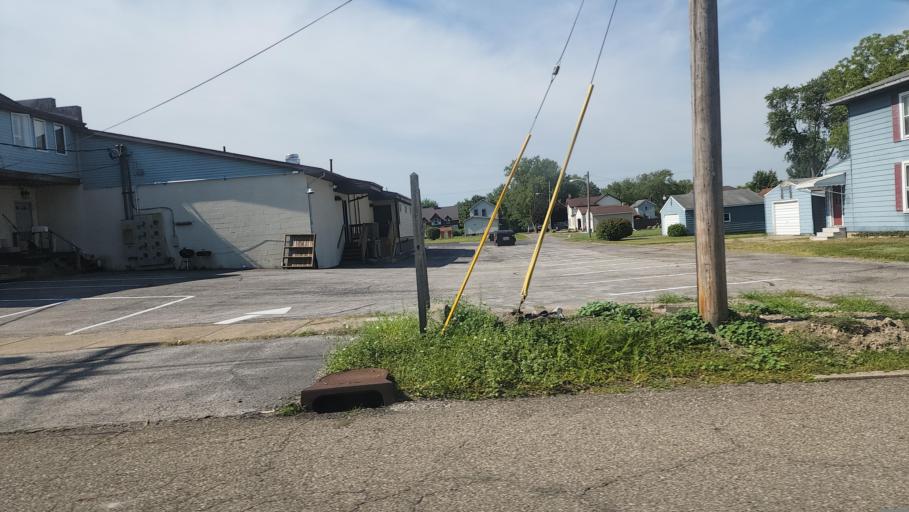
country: US
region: Ohio
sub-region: Trumbull County
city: Niles
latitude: 41.1872
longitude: -80.7564
